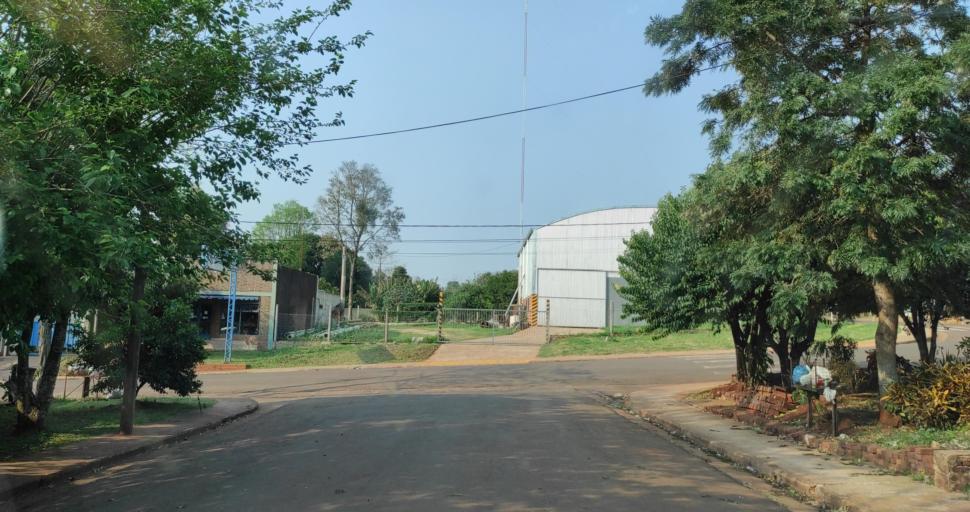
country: AR
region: Misiones
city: Cerro Azul
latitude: -27.6357
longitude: -55.4945
